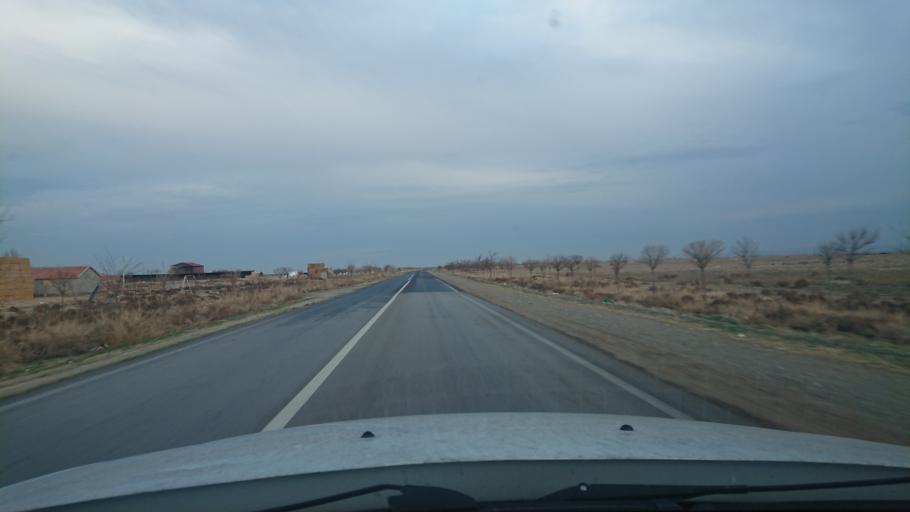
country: TR
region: Aksaray
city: Yesilova
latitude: 38.3047
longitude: 33.7557
